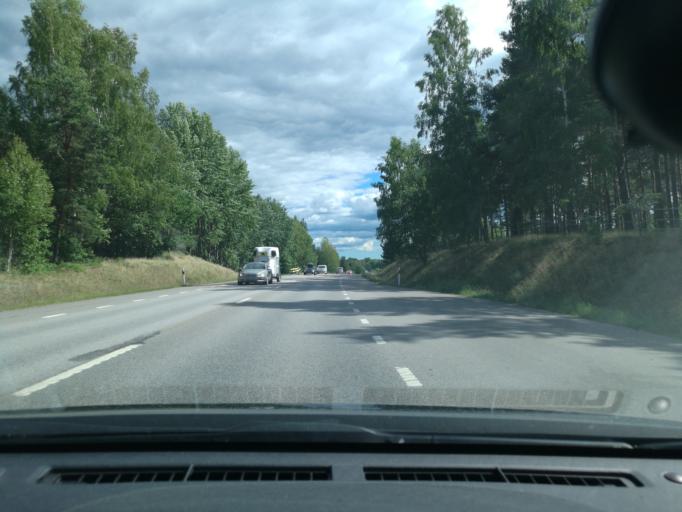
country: SE
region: OEstergoetland
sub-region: Soderkopings Kommun
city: Soederkoeping
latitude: 58.4598
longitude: 16.3640
